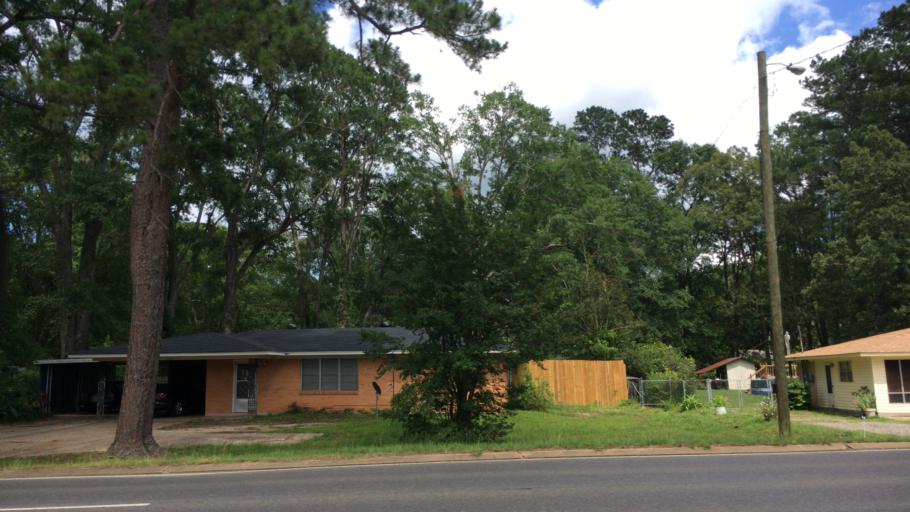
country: US
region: Louisiana
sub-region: Lincoln Parish
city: Ruston
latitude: 32.5127
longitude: -92.6382
